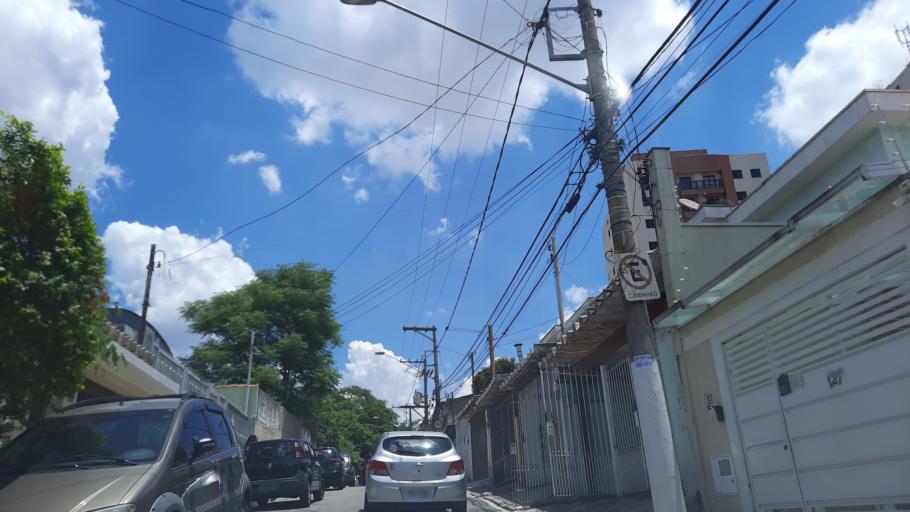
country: BR
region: Sao Paulo
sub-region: Sao Paulo
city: Sao Paulo
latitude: -23.4903
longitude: -46.6811
